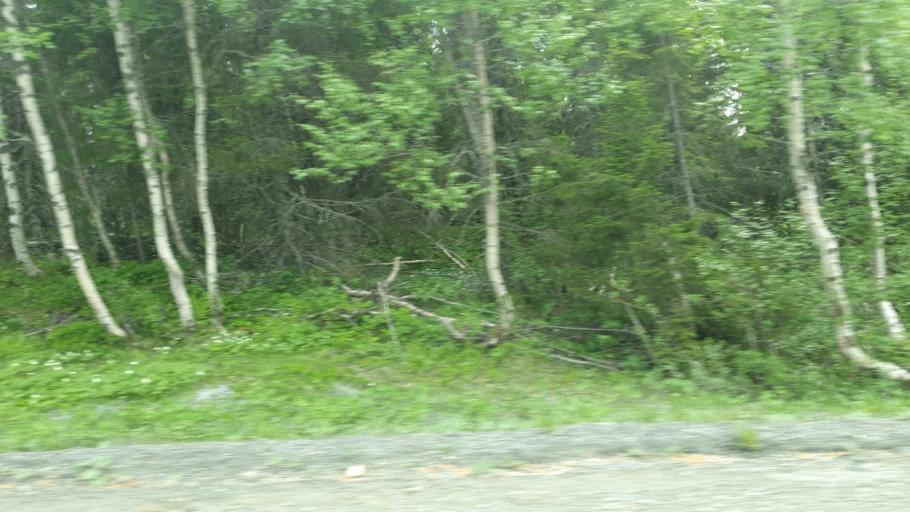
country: NO
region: Nord-Trondelag
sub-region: Leksvik
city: Leksvik
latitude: 63.6874
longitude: 10.4004
